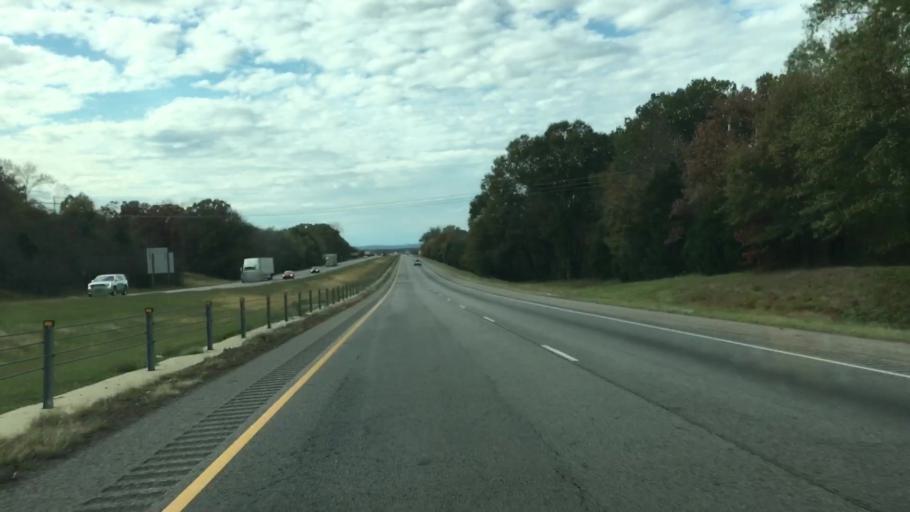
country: US
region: Arkansas
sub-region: Conway County
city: Morrilton
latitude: 35.1822
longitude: -92.7634
